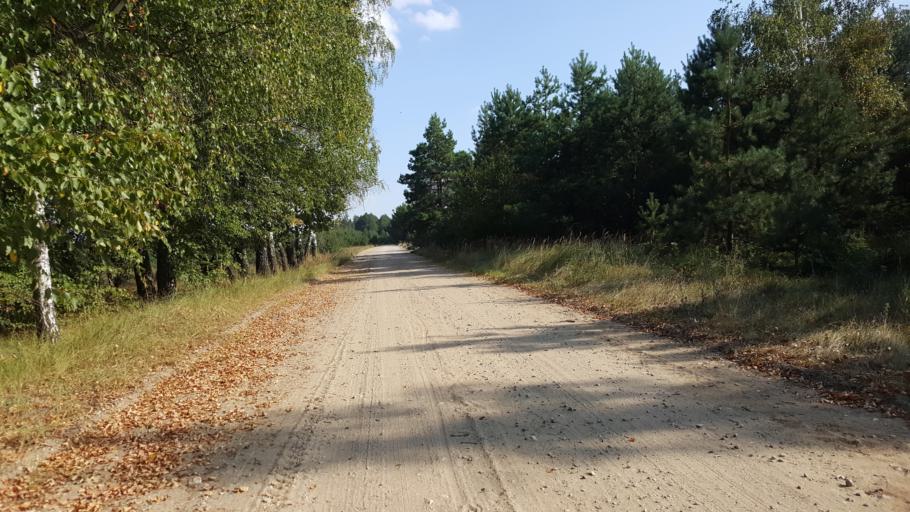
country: BY
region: Brest
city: Kamyanyuki
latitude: 52.5602
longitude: 23.6416
